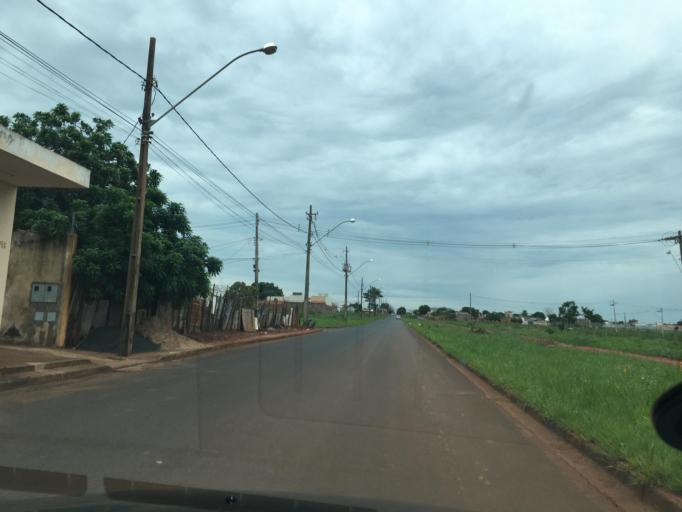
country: BR
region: Minas Gerais
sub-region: Uberlandia
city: Uberlandia
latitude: -18.8655
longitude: -48.2230
